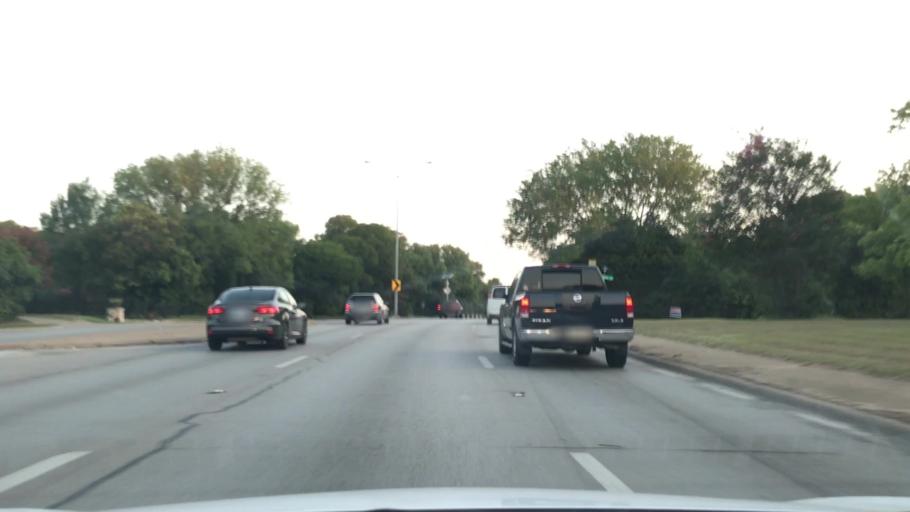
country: US
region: Texas
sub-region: Dallas County
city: Highland Park
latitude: 32.8251
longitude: -96.6967
